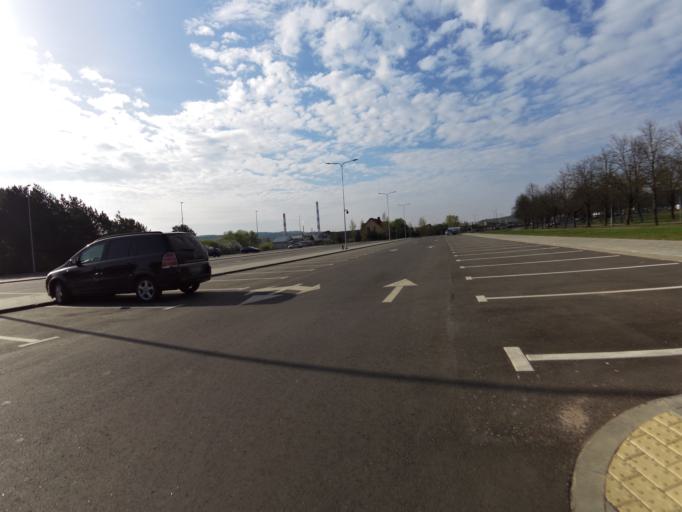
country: LT
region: Vilnius County
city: Vilkpede
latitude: 54.6753
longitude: 25.2278
